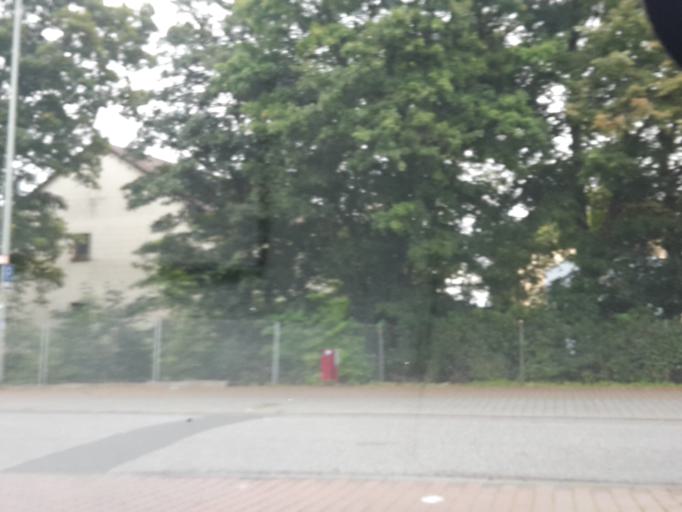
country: DE
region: Hesse
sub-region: Regierungsbezirk Darmstadt
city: Idstein
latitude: 50.2173
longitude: 8.2585
